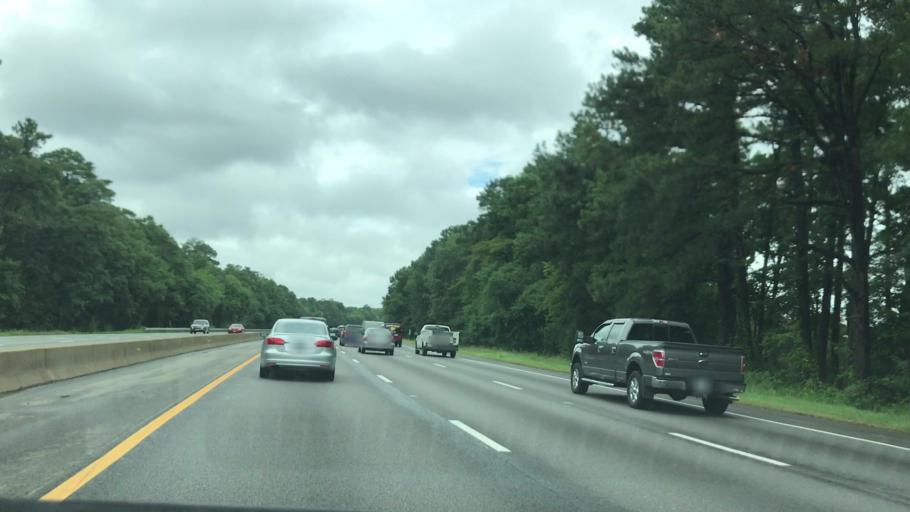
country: US
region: Virginia
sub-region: Chesterfield County
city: Chester
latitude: 37.3869
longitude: -77.4193
